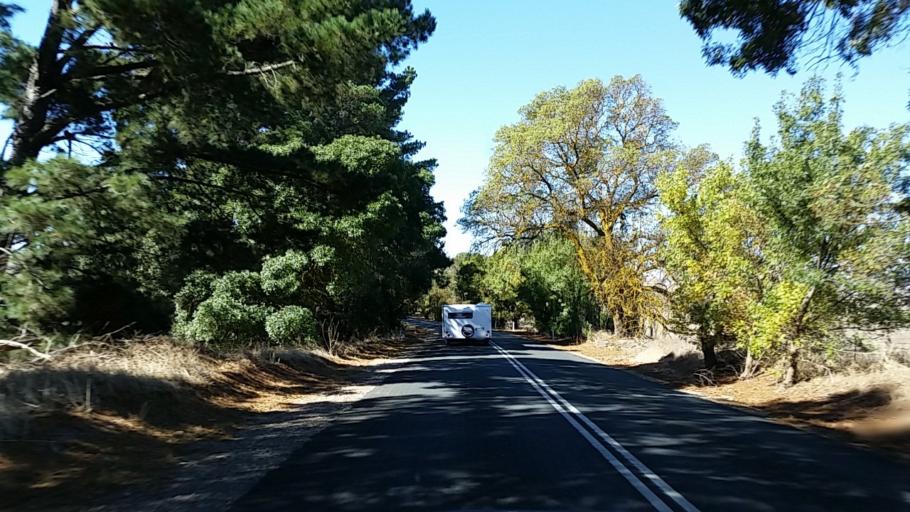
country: AU
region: South Australia
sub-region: Adelaide Hills
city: Birdwood
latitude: -34.7732
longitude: 139.0731
